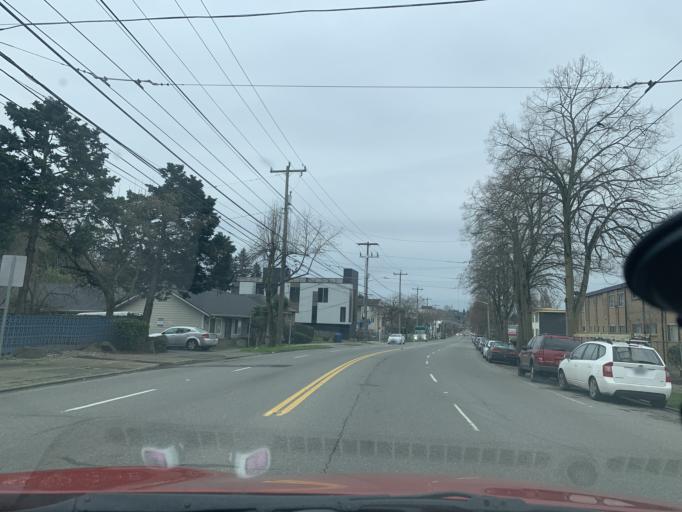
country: US
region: Washington
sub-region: King County
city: Bryn Mawr-Skyway
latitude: 47.5361
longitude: -122.2701
